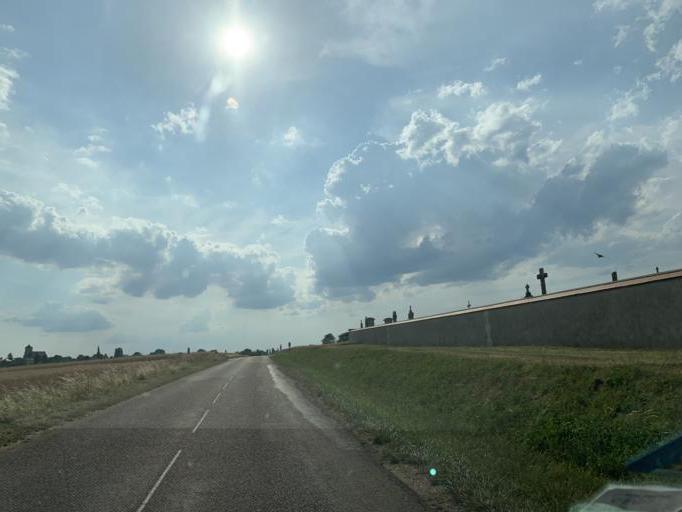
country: FR
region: Bourgogne
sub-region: Departement de l'Yonne
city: Fontenailles
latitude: 47.5066
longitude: 3.3582
